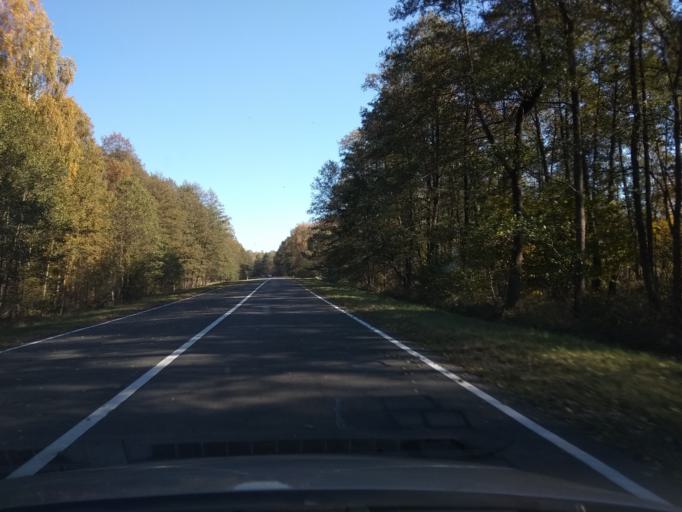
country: BY
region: Brest
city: Kobryn
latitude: 52.0310
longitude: 24.2644
